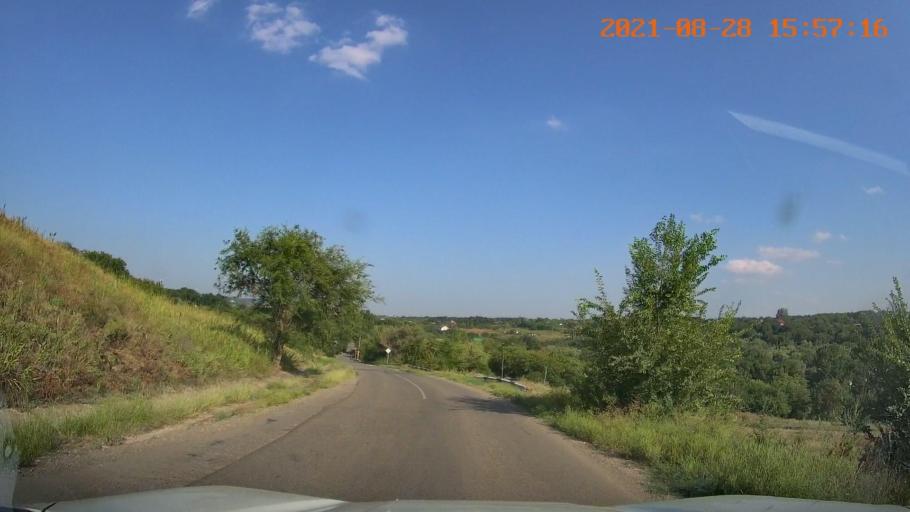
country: RU
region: Stavropol'skiy
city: Tatarka
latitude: 44.9602
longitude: 41.9388
